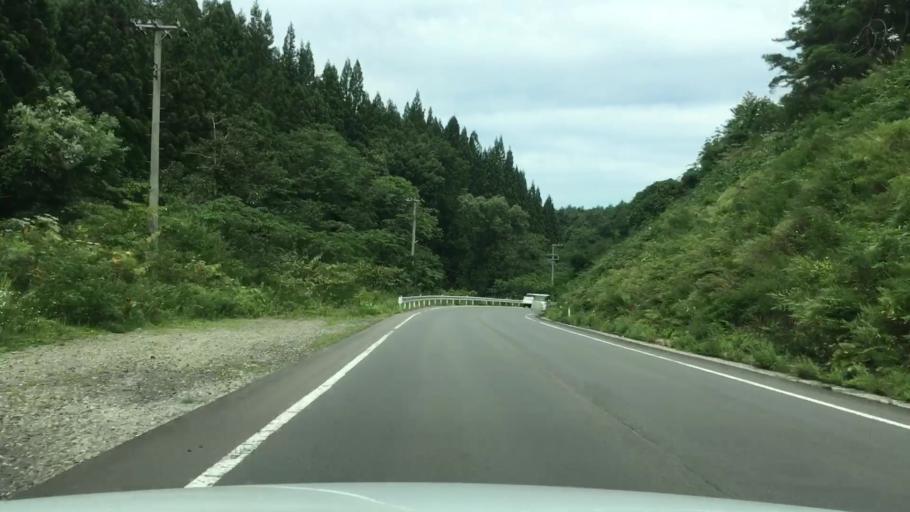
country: JP
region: Aomori
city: Shimokizukuri
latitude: 40.7264
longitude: 140.2541
